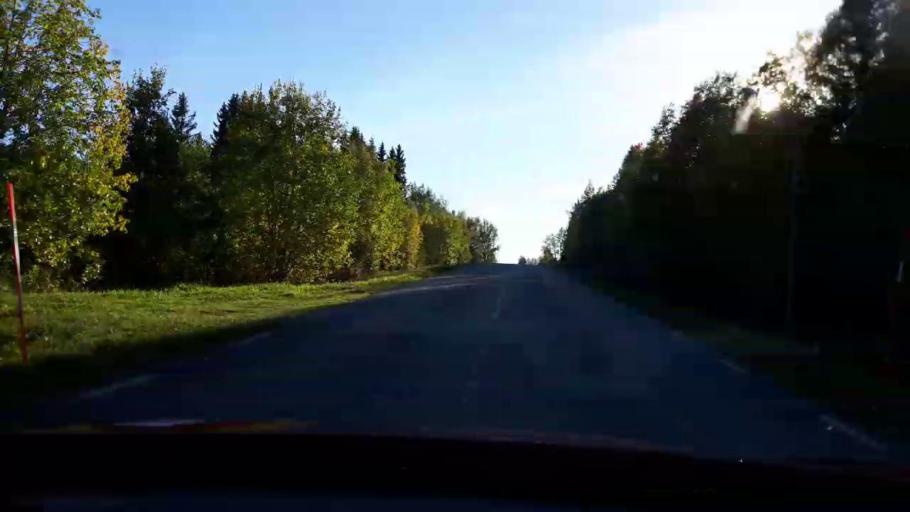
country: SE
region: Jaemtland
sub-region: OEstersunds Kommun
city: Lit
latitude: 63.8179
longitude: 14.8143
